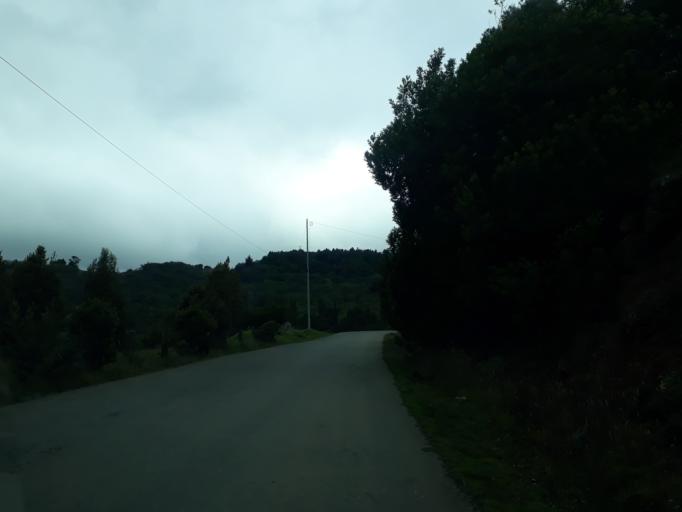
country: CO
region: Cundinamarca
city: Cucunuba
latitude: 5.1974
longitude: -73.7887
